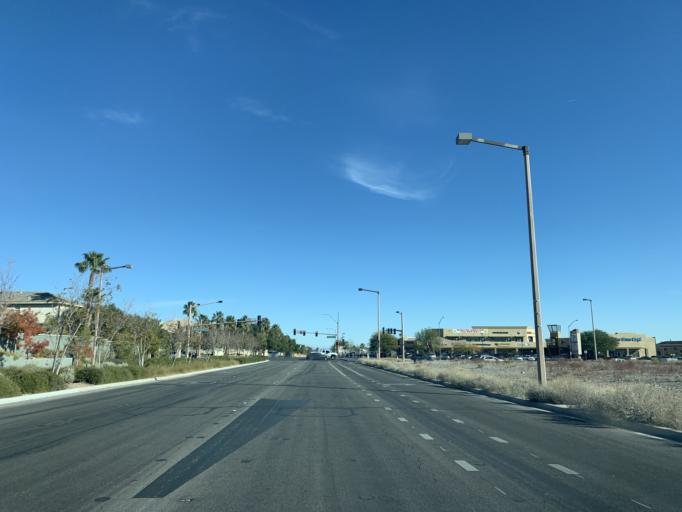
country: US
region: Nevada
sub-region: Clark County
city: Summerlin South
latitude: 36.1225
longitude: -115.3164
